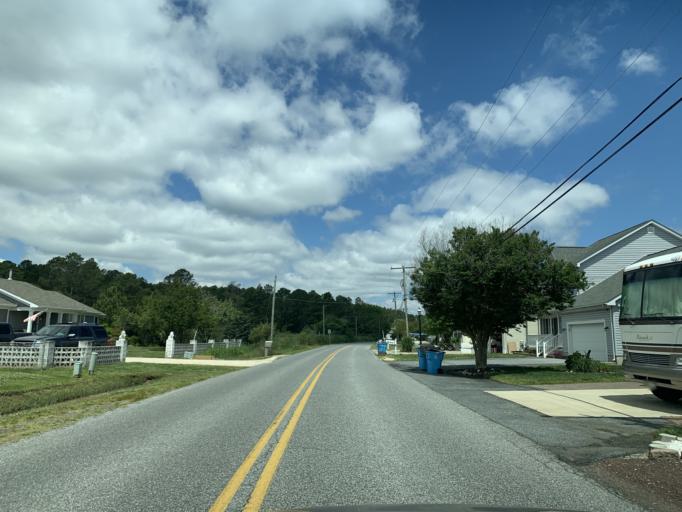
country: US
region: Maryland
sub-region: Worcester County
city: West Ocean City
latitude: 38.3547
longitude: -75.1189
